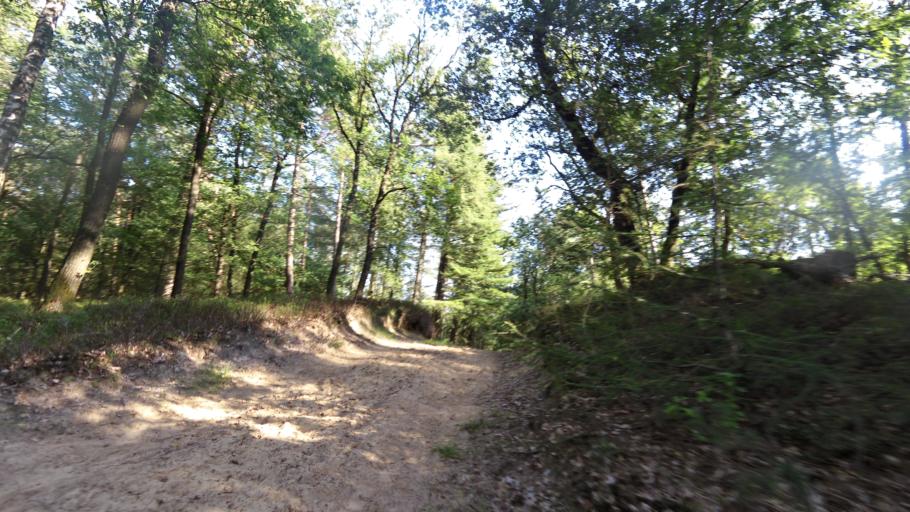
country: NL
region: Gelderland
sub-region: Gemeente Apeldoorn
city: Loenen
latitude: 52.1204
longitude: 5.9849
